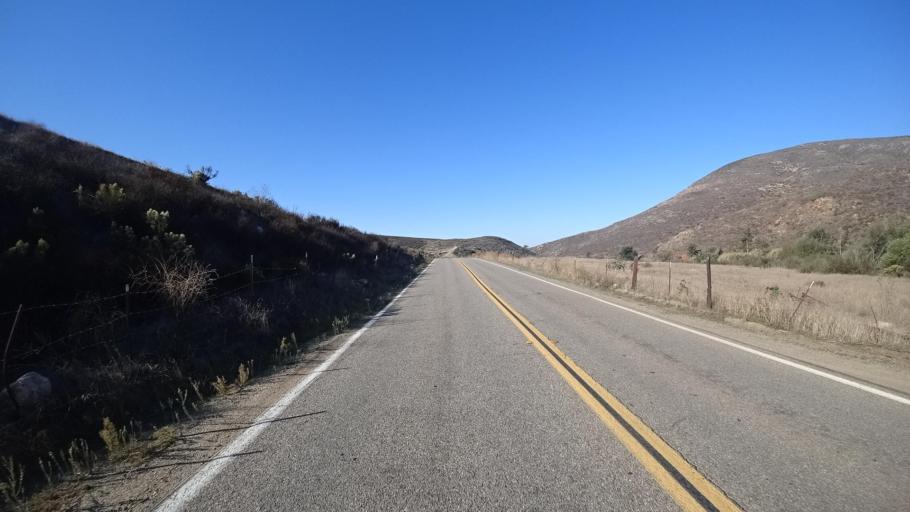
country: US
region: California
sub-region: San Diego County
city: Jamul
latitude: 32.6431
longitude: -116.8712
